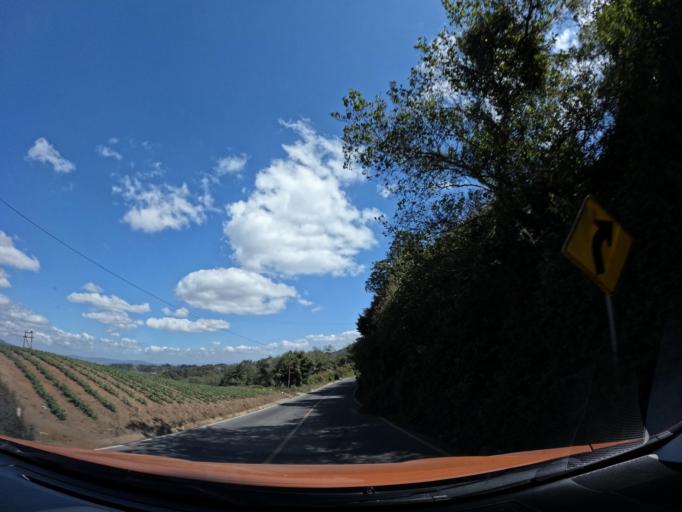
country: GT
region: Chimaltenango
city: Patzun
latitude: 14.6490
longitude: -91.0454
